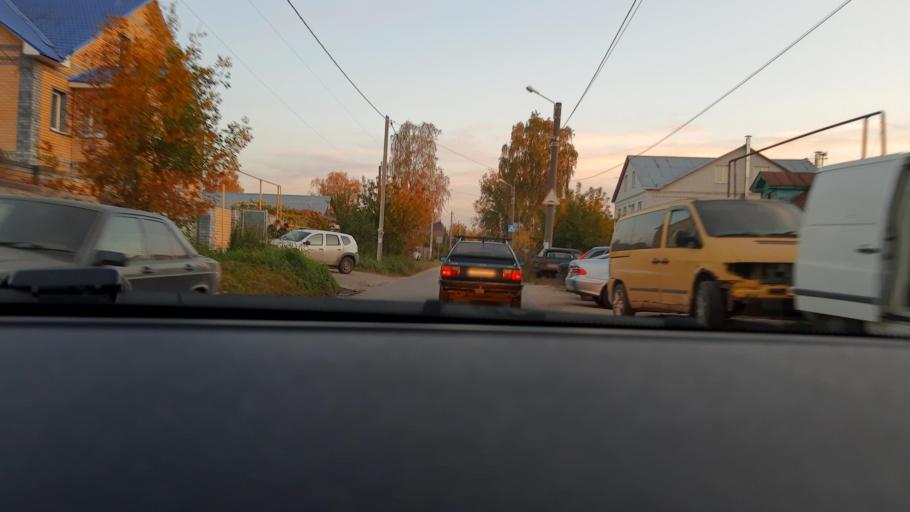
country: RU
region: Nizjnij Novgorod
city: Gorbatovka
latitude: 56.3338
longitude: 43.8307
